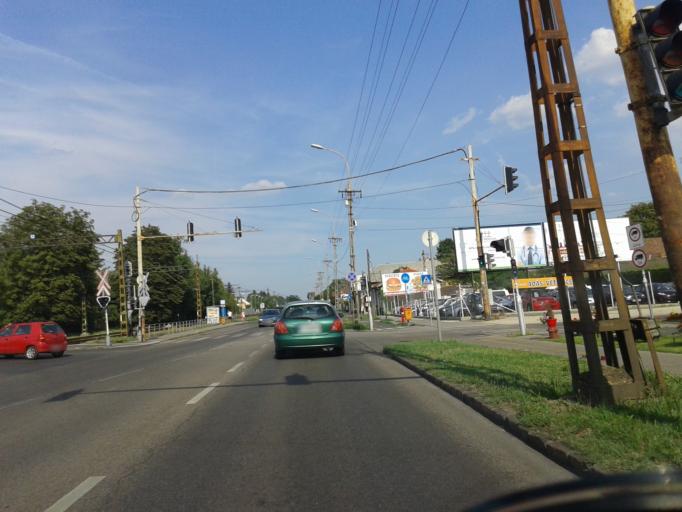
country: HU
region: Budapest
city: Budapest XVI. keruelet
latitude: 47.5076
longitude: 19.1721
